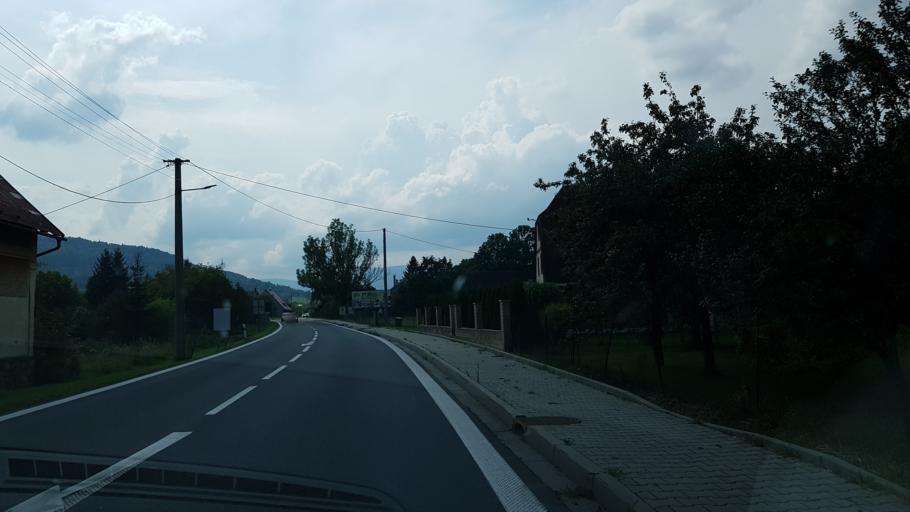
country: CZ
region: Olomoucky
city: Pisecna
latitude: 50.2680
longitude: 17.2444
